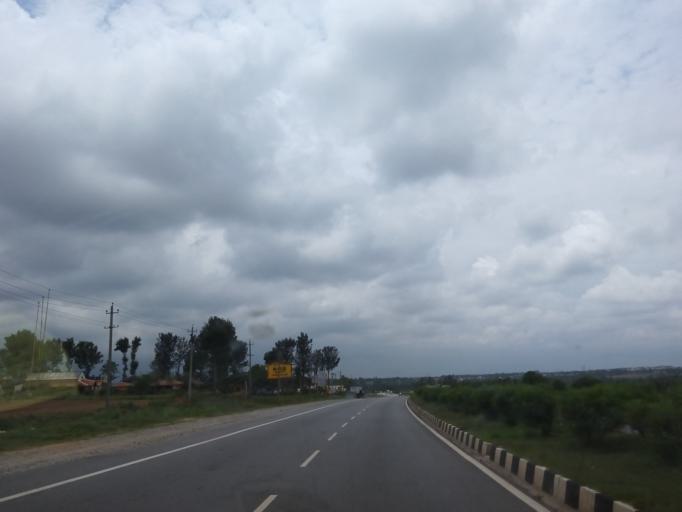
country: IN
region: Karnataka
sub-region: Hassan
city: Hassan
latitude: 12.9943
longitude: 76.1617
